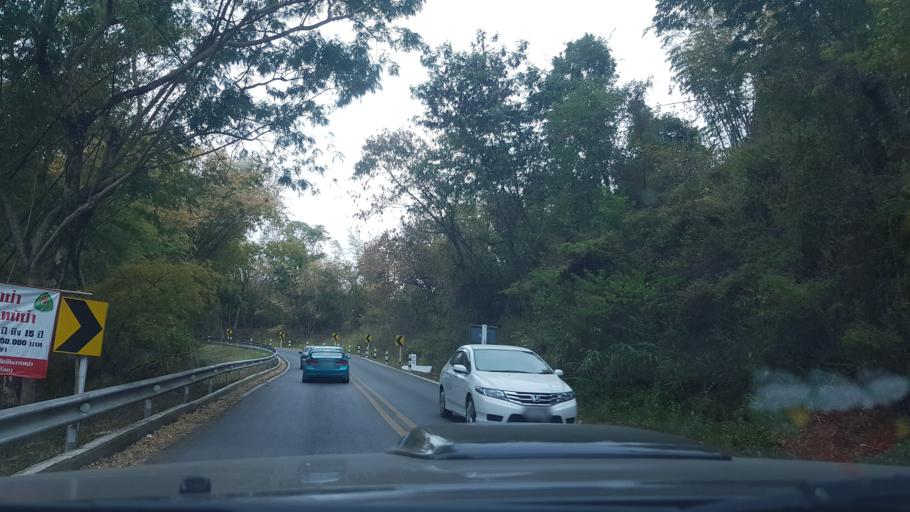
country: TH
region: Phetchabun
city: Khao Kho
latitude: 16.5477
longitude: 101.0381
